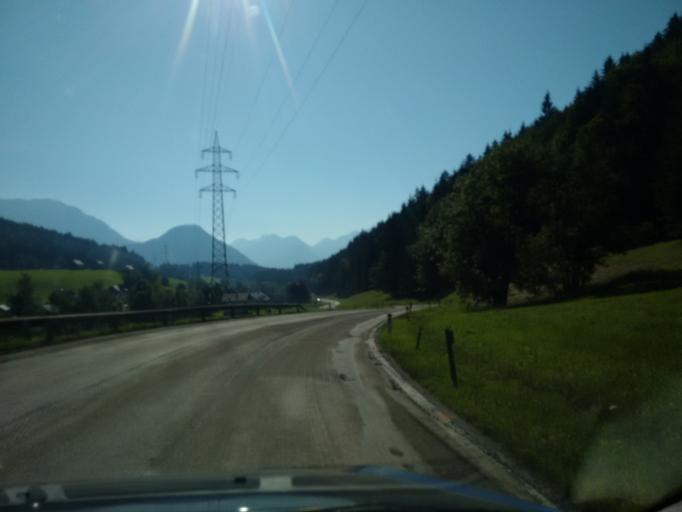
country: AT
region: Styria
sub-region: Politischer Bezirk Liezen
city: Altaussee
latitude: 47.6268
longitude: 13.7302
